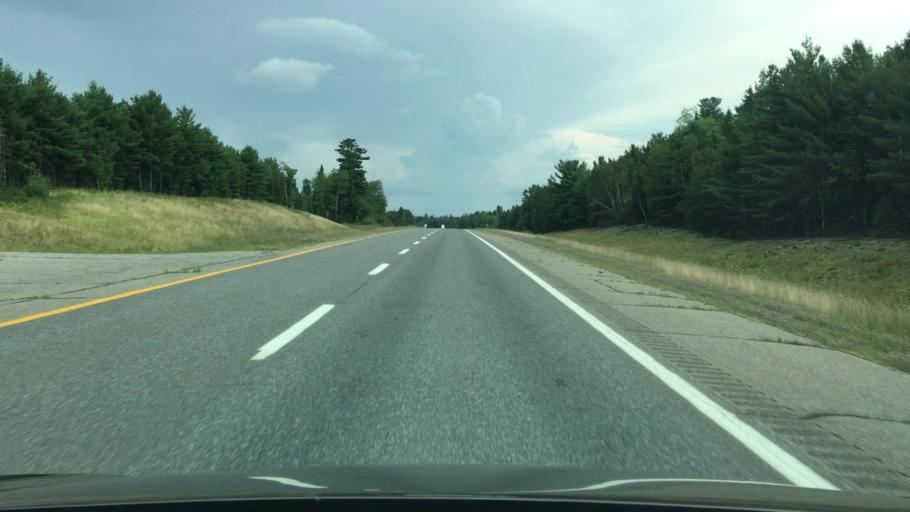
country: US
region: Maine
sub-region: Penobscot County
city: Medway
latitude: 45.4969
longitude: -68.5607
